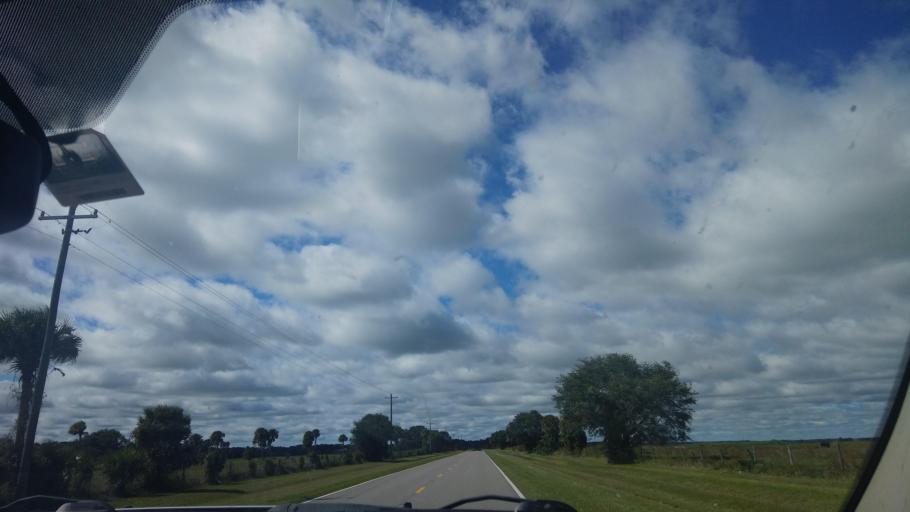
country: US
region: Florida
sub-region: Okeechobee County
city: Okeechobee
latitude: 27.3948
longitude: -80.9040
